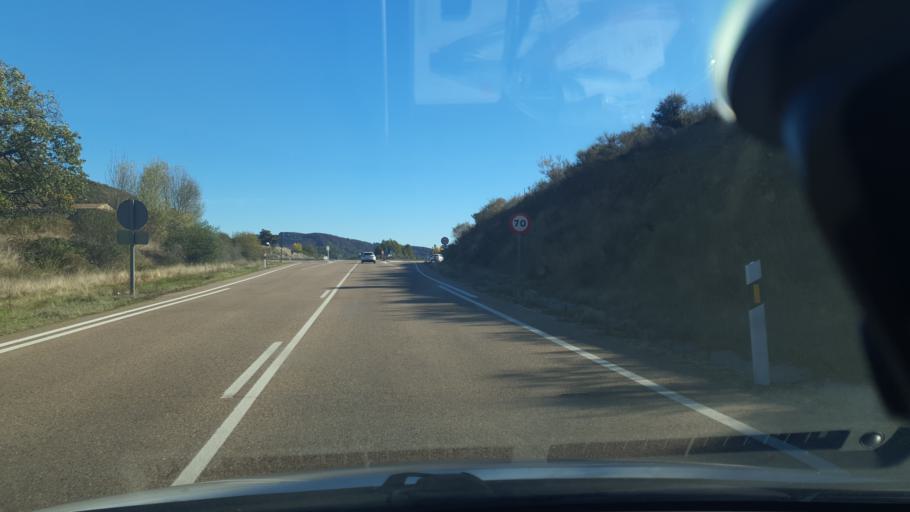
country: ES
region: Castille and Leon
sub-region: Provincia de Avila
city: Poyales del Hoyo
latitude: 40.1574
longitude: -5.1717
